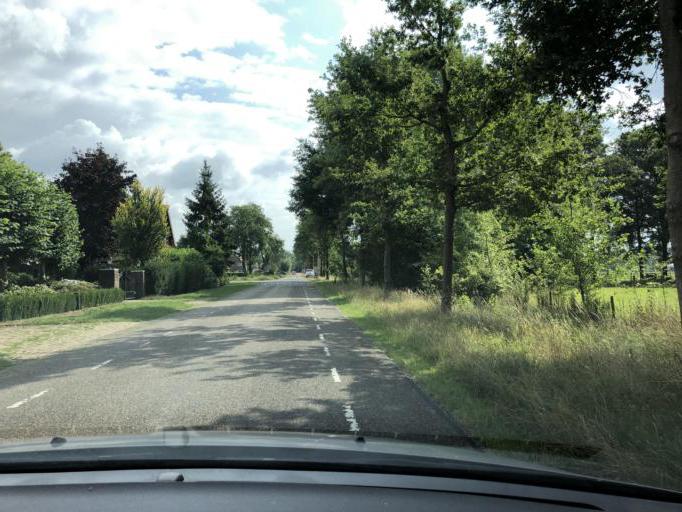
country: NL
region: Overijssel
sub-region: Gemeente Dalfsen
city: Dalfsen
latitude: 52.5787
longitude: 6.3430
